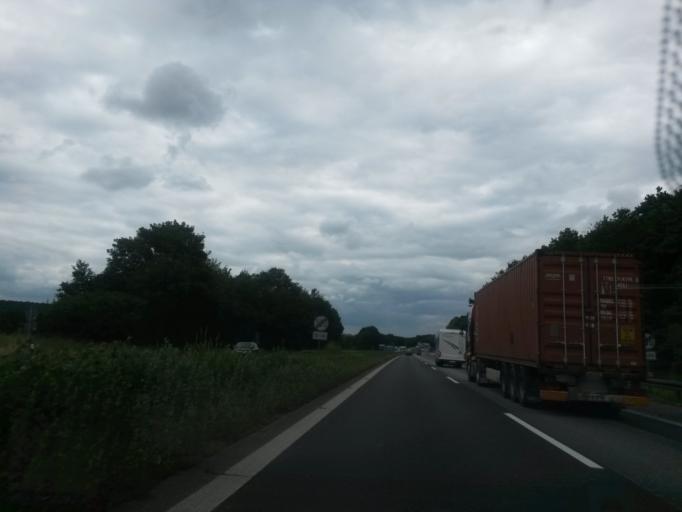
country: DE
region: Bavaria
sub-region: Regierungsbezirk Unterfranken
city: Geiselwind
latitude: 49.7695
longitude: 10.4823
